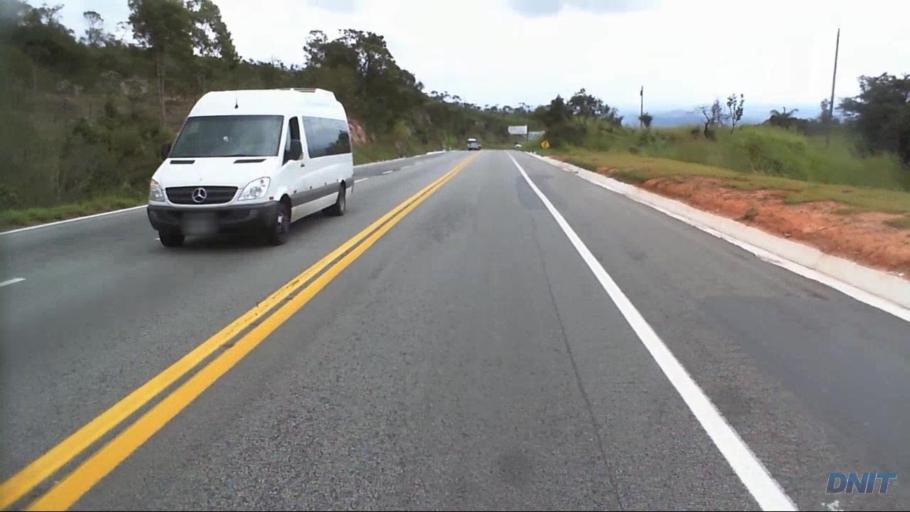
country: BR
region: Minas Gerais
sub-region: Caete
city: Caete
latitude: -19.7886
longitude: -43.7071
